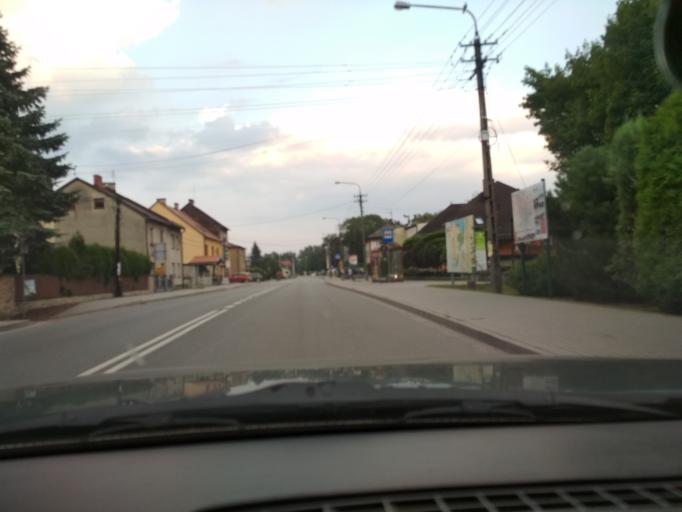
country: PL
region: Silesian Voivodeship
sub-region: Powiat cieszynski
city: Mnich
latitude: 49.8948
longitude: 18.8139
